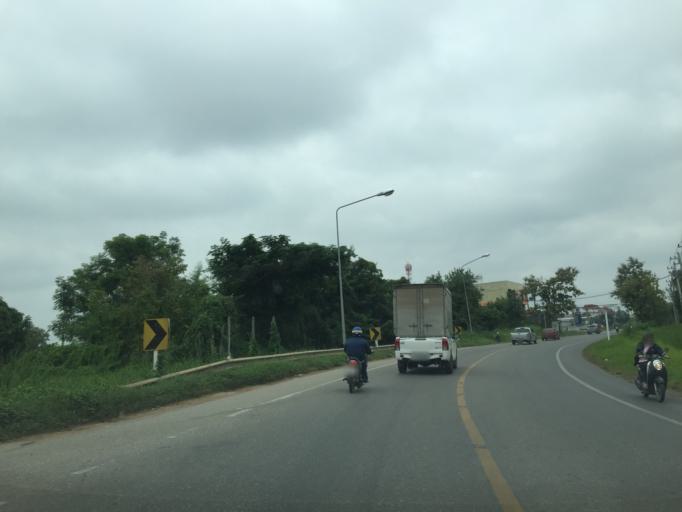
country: TH
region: Lamphun
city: Lamphun
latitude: 18.5828
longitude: 99.0586
